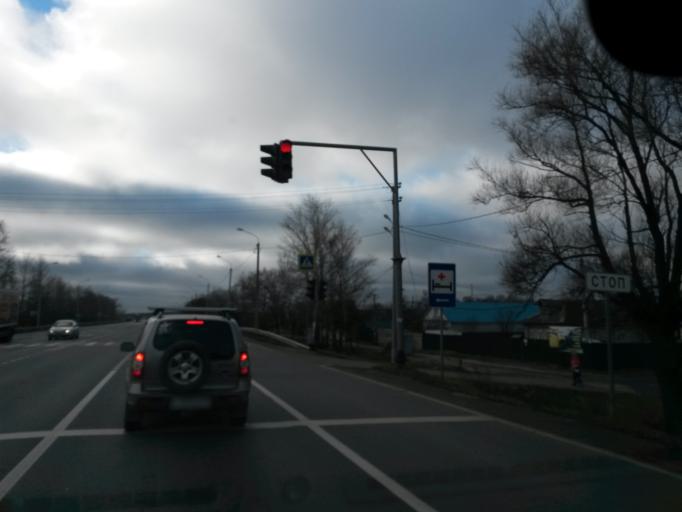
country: RU
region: Jaroslavl
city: Semibratovo
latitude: 57.3015
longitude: 39.5363
